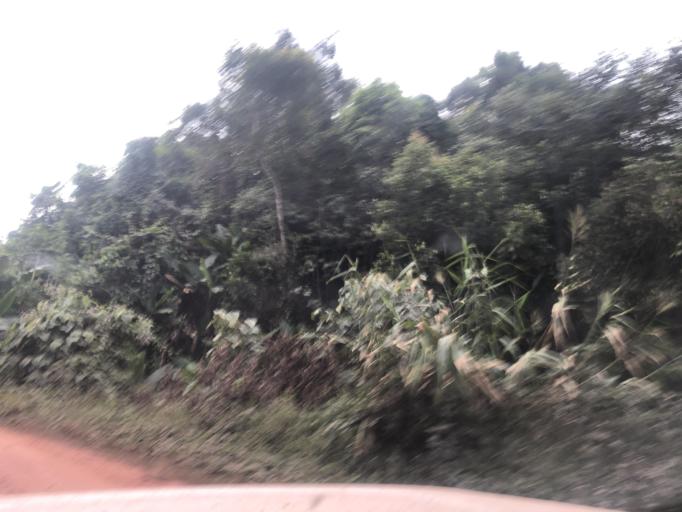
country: CN
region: Yunnan
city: Menglie
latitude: 22.1257
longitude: 101.7593
